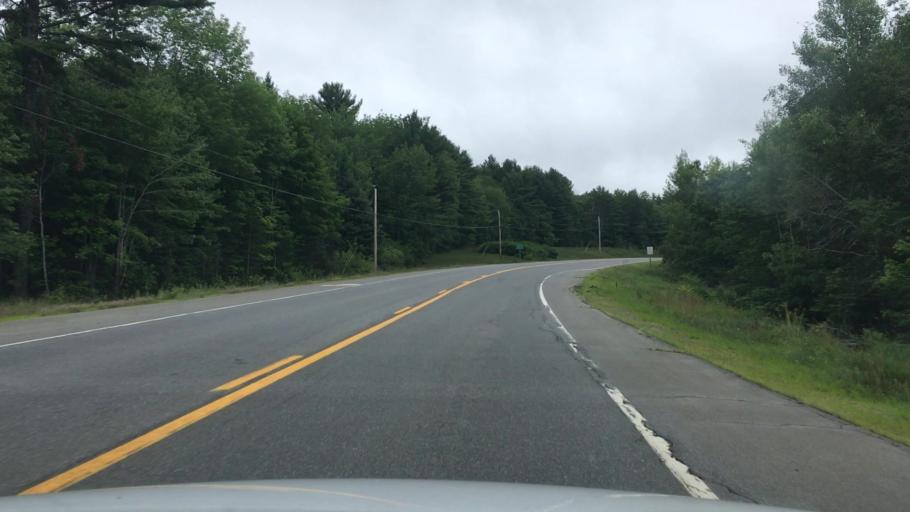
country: US
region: Maine
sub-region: Hancock County
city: Franklin
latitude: 44.8402
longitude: -68.1525
